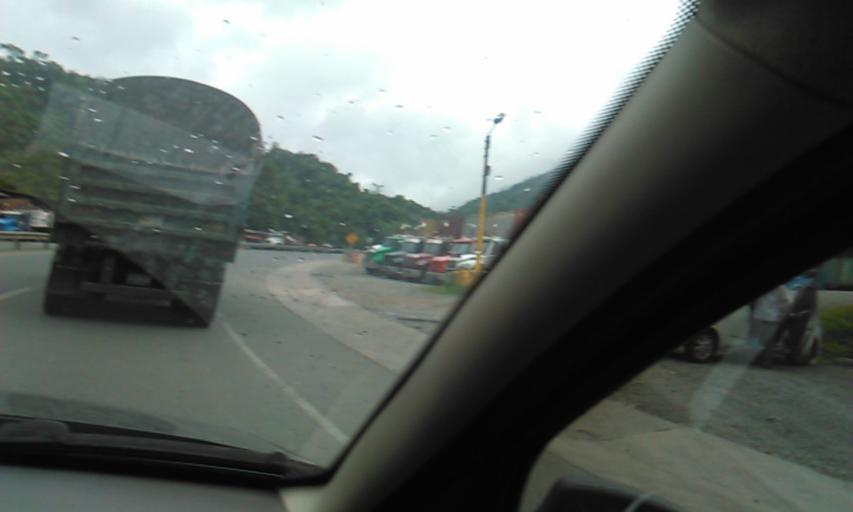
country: CO
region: Valle del Cauca
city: Dagua
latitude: 3.8447
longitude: -76.7933
